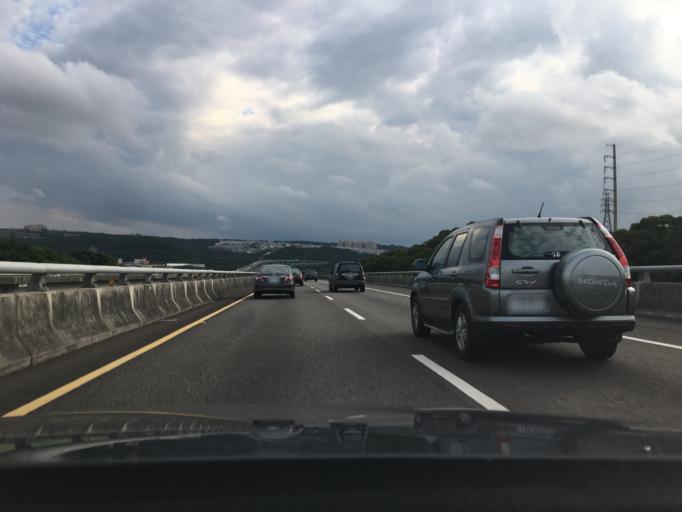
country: TW
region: Taiwan
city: Daxi
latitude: 24.9209
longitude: 121.1683
